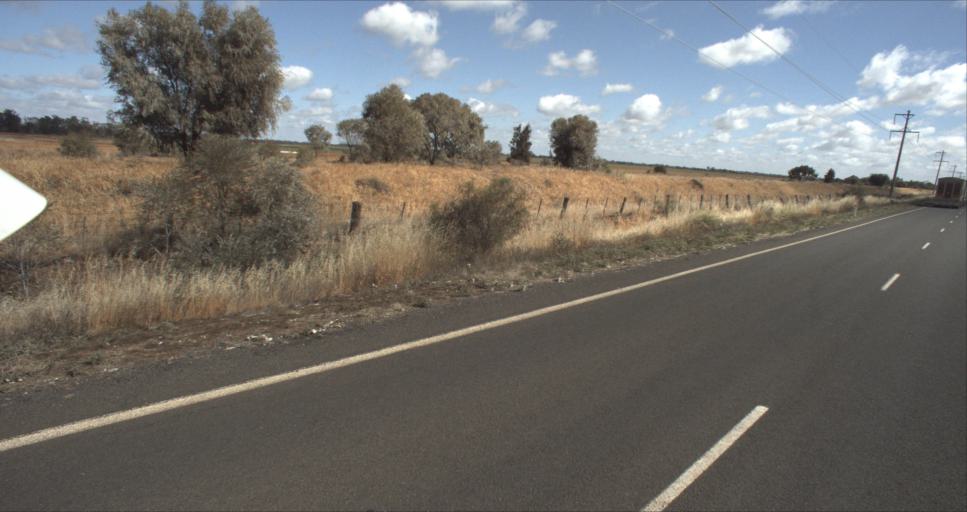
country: AU
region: New South Wales
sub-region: Murrumbidgee Shire
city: Darlington Point
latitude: -34.5403
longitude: 146.1723
